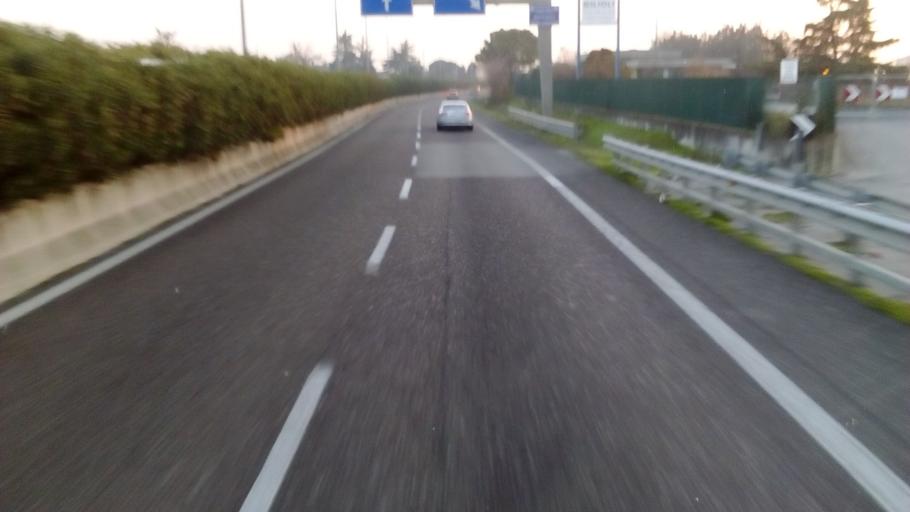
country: IT
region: Lombardy
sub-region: Provincia di Brescia
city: Desenzano del Garda
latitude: 45.4378
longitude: 10.5175
